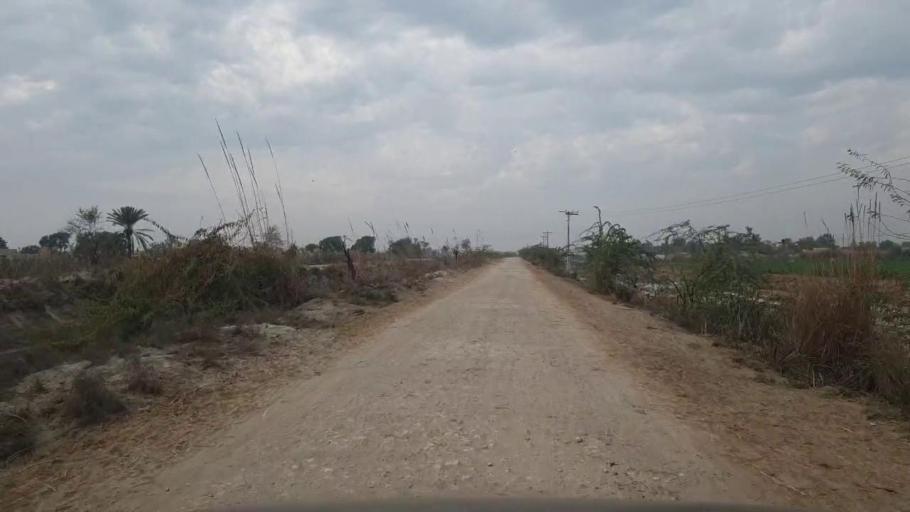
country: PK
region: Sindh
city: Sakrand
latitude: 26.0928
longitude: 68.3999
